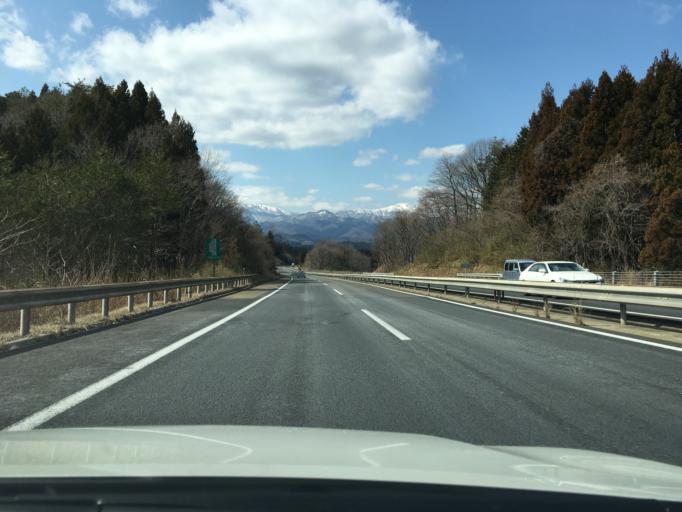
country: JP
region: Miyagi
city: Okawara
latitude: 38.1648
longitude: 140.6549
